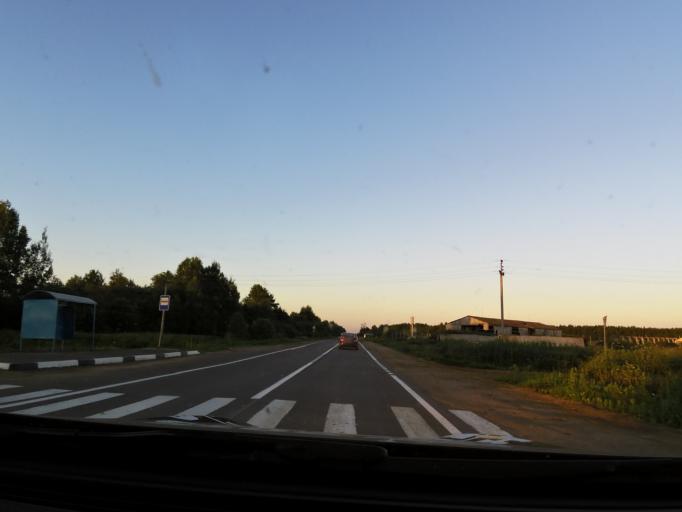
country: RU
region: Jaroslavl
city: Lyubim
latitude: 58.3585
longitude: 40.5523
